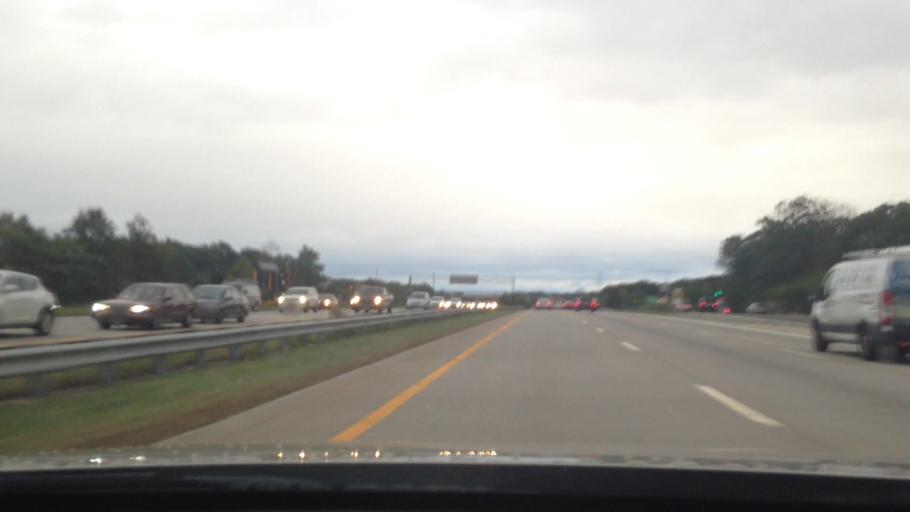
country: US
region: New York
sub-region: Suffolk County
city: Bohemia
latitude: 40.7634
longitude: -73.0881
